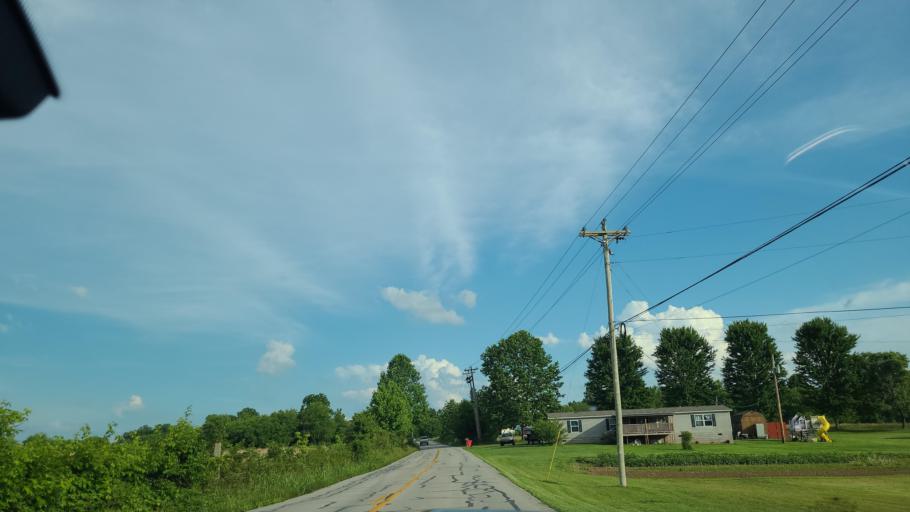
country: US
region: Kentucky
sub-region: Whitley County
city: Corbin
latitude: 36.9001
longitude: -84.2353
